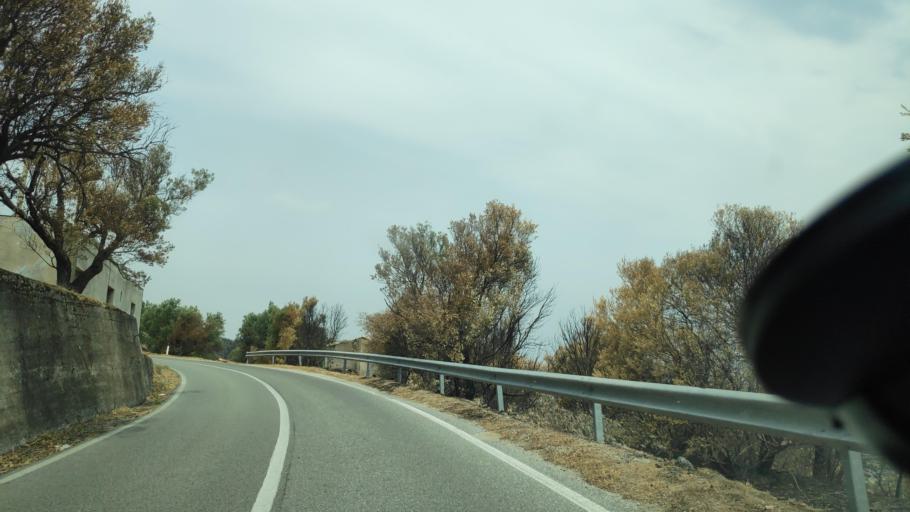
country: IT
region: Calabria
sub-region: Provincia di Catanzaro
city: Sant'Andrea Apostolo dello Ionio
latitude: 38.6455
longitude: 16.5309
